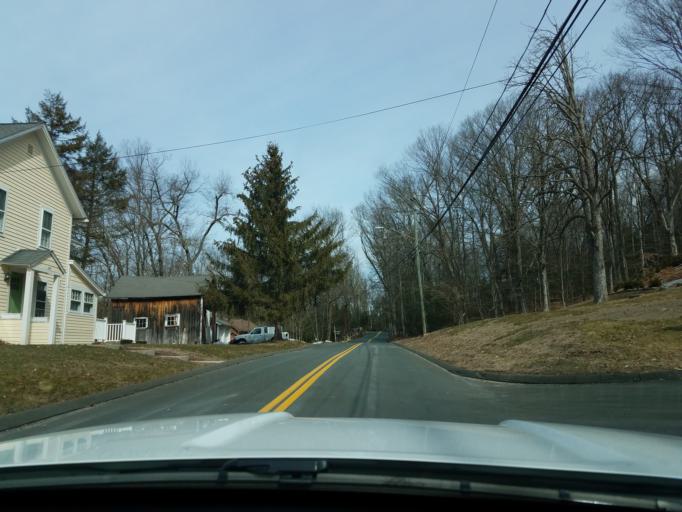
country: US
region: Connecticut
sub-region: Hartford County
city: Collinsville
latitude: 41.7911
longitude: -72.9220
